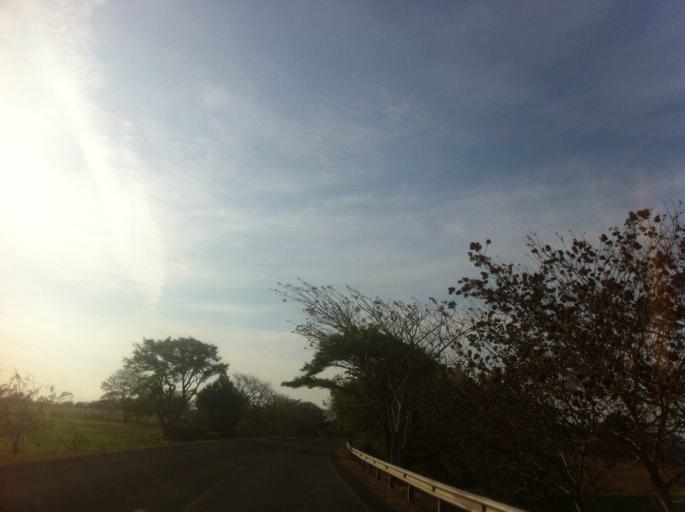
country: NI
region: Rivas
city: Cardenas
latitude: 11.2892
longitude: -85.6789
